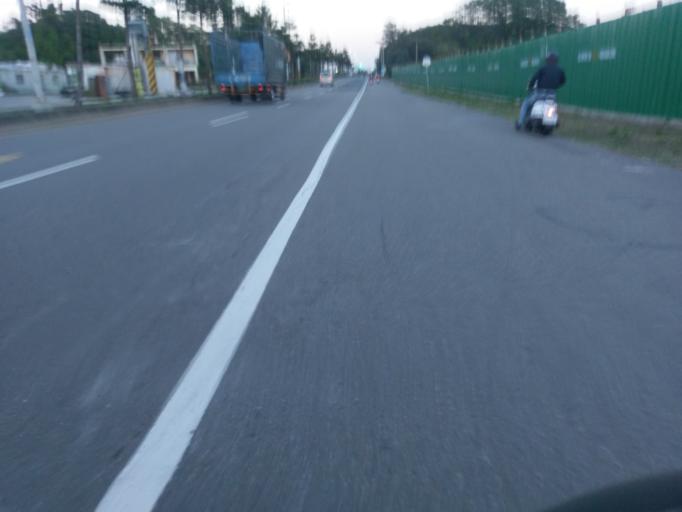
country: TW
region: Taiwan
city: Taoyuan City
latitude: 25.0549
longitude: 121.1384
